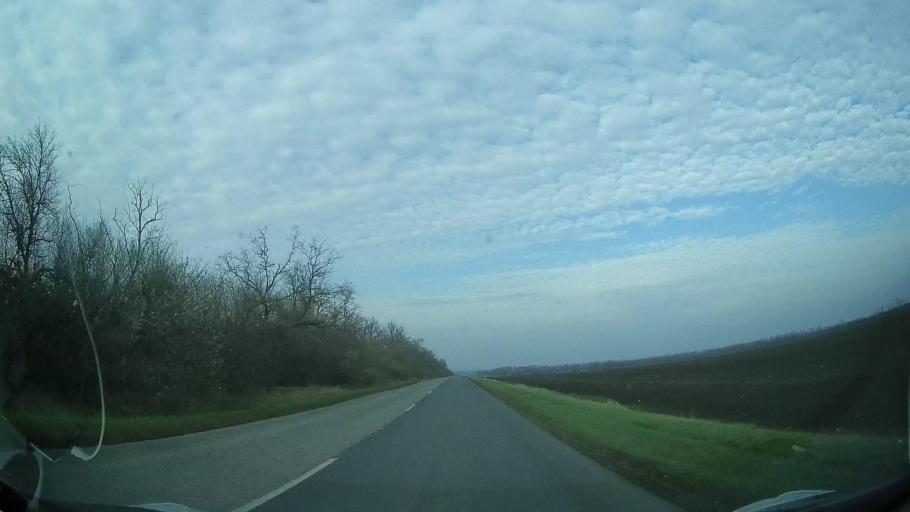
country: RU
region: Rostov
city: Bagayevskaya
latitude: 47.0827
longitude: 40.3915
